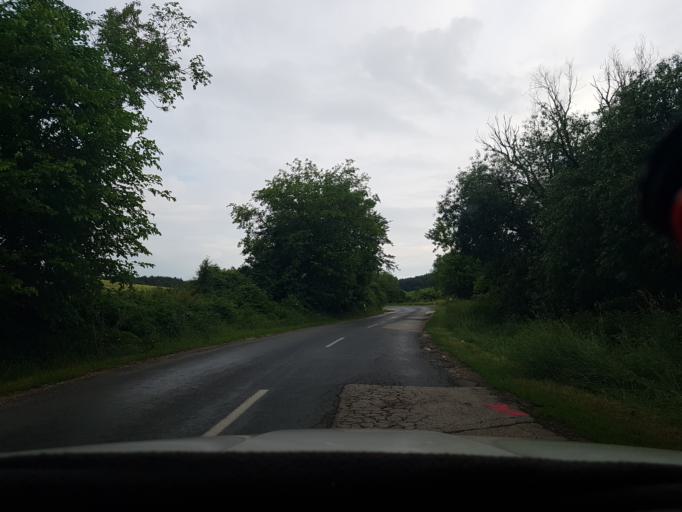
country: HU
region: Pest
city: Perbal
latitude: 47.6352
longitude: 18.7554
